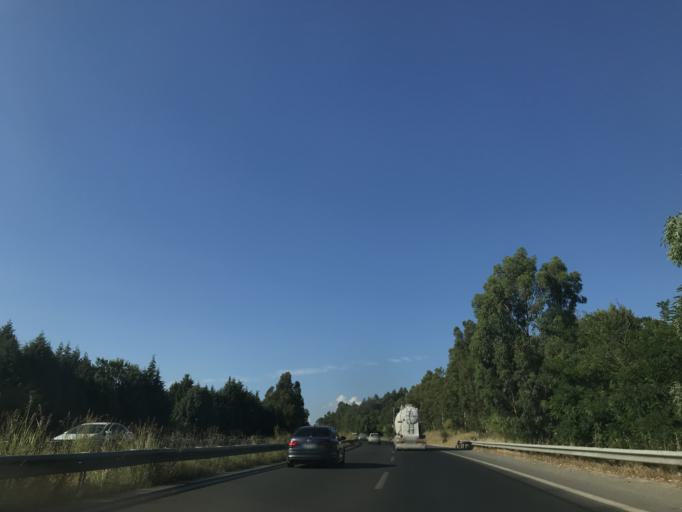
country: TR
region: Aydin
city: Ortaklar
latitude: 37.8397
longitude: 27.5398
